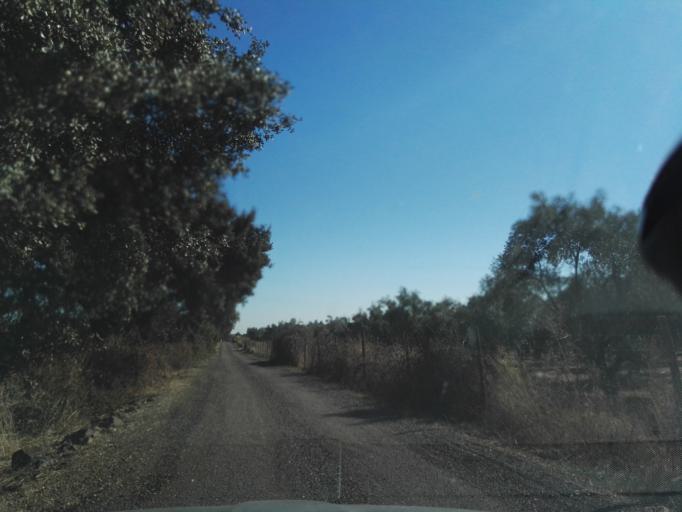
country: PT
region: Portalegre
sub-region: Elvas
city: Elvas
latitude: 38.9187
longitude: -7.1751
